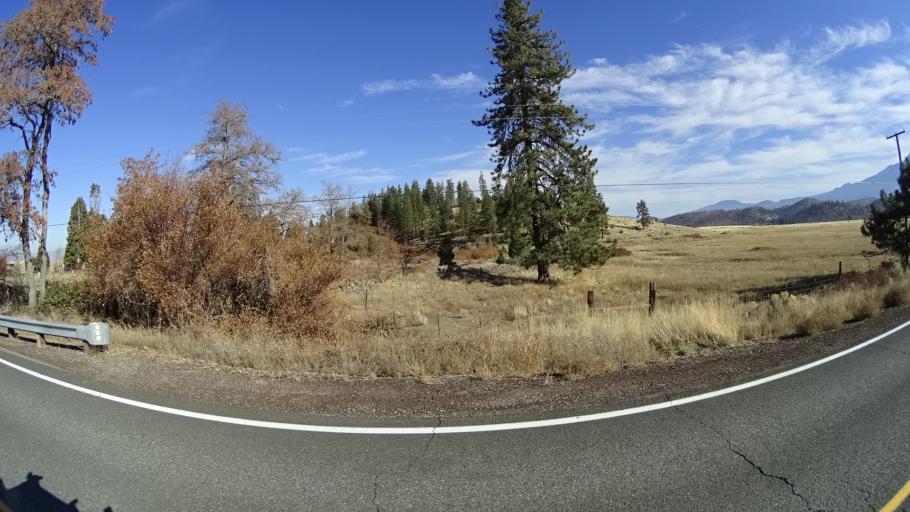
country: US
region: California
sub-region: Siskiyou County
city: Weed
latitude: 41.4476
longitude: -122.4493
